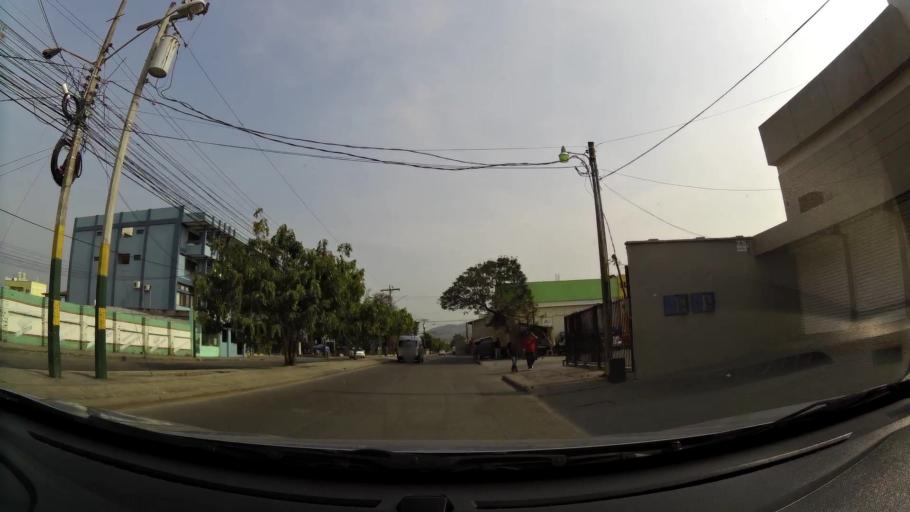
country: HN
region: Comayagua
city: Comayagua
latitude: 14.4586
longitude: -87.6445
